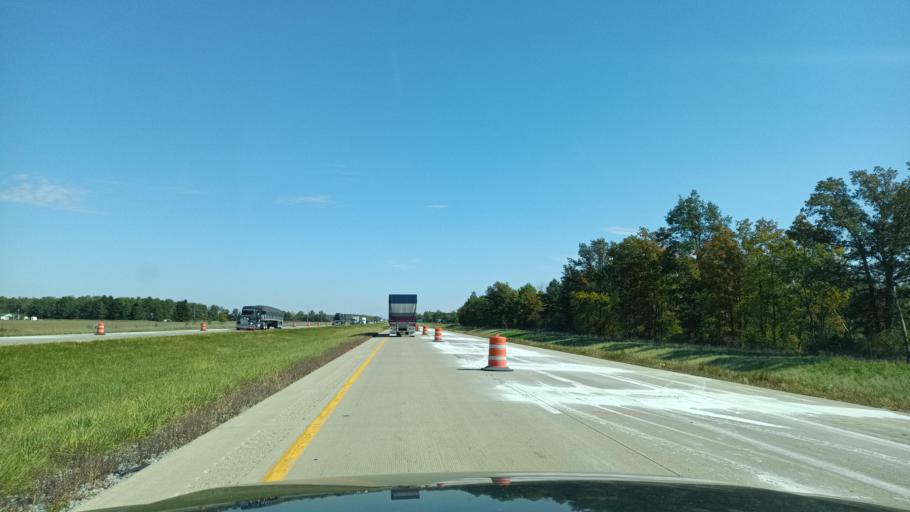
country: US
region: Ohio
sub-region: Paulding County
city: Paulding
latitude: 41.2347
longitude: -84.5394
